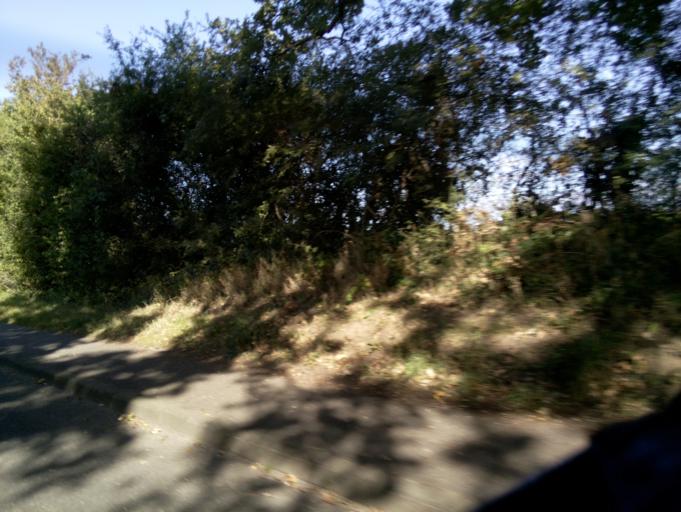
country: GB
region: England
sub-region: West Berkshire
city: Cold Ash
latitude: 51.4156
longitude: -1.2621
